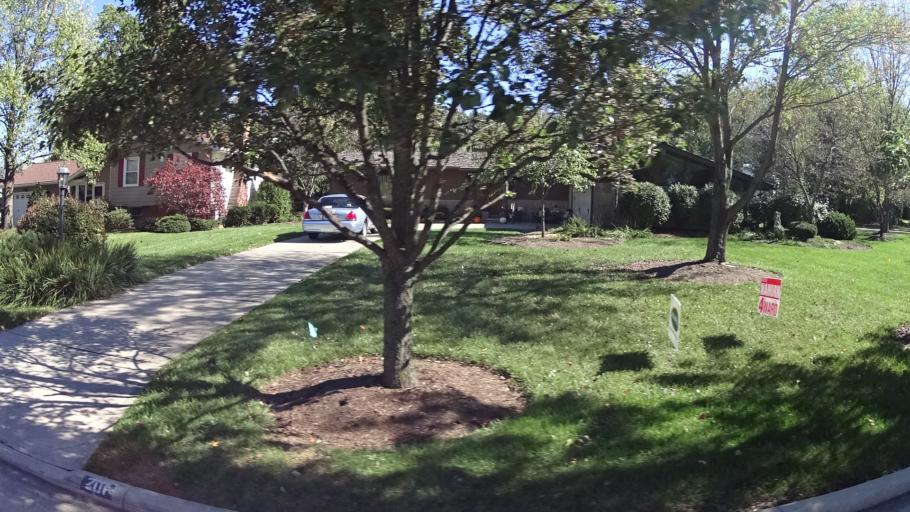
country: US
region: Ohio
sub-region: Lorain County
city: Amherst
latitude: 41.4059
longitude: -82.2145
